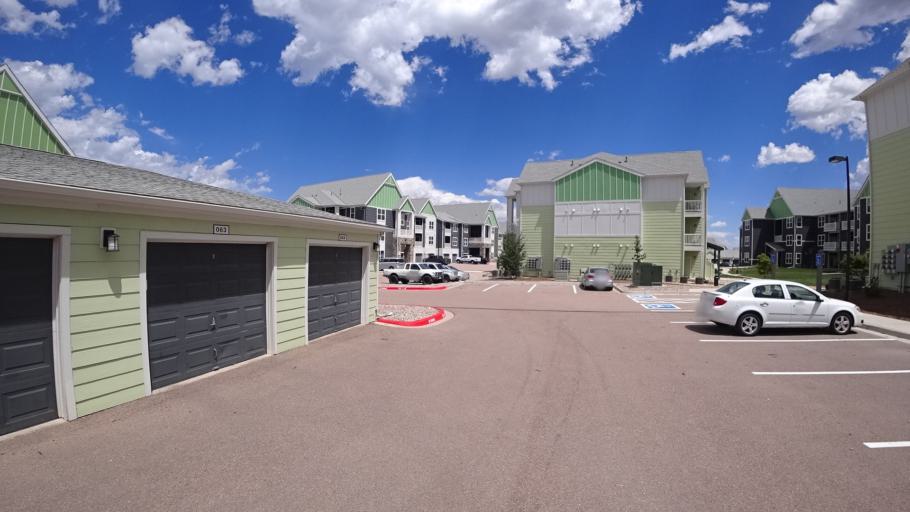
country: US
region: Colorado
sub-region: El Paso County
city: Black Forest
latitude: 38.9434
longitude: -104.7100
